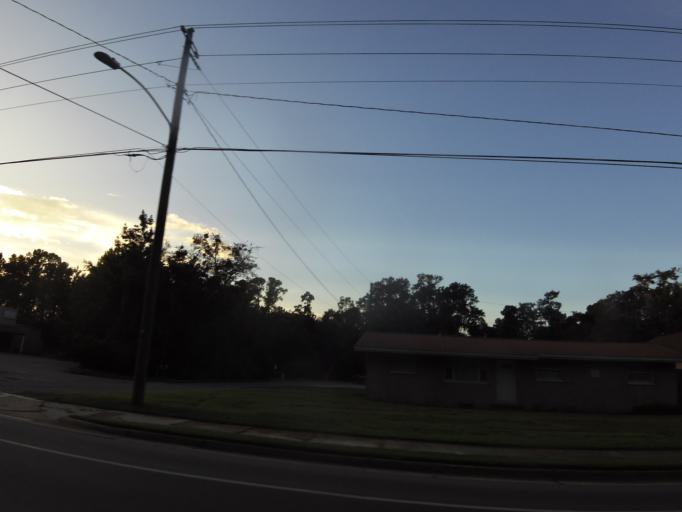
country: US
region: Georgia
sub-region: Camden County
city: Kingsland
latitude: 30.7995
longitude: -81.6938
